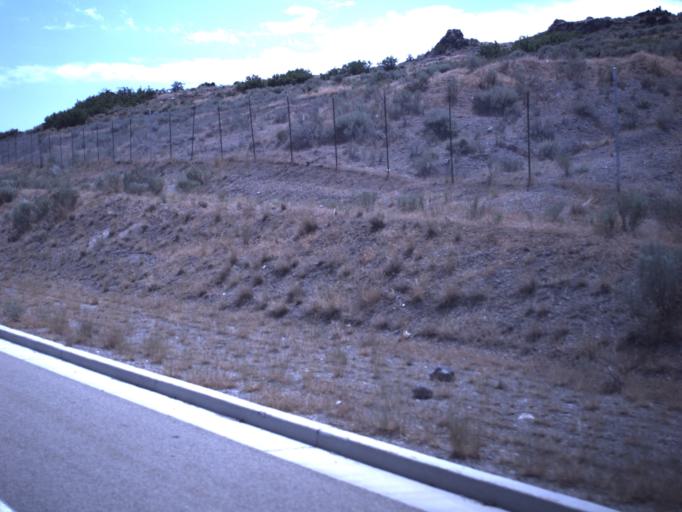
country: US
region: Utah
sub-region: Salt Lake County
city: Bluffdale
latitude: 40.4712
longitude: -111.9706
